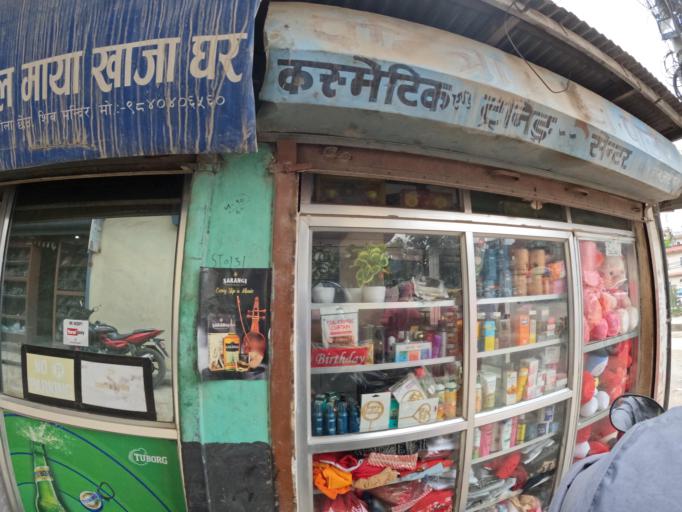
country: NP
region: Central Region
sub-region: Bagmati Zone
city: Kathmandu
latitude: 27.7402
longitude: 85.3123
